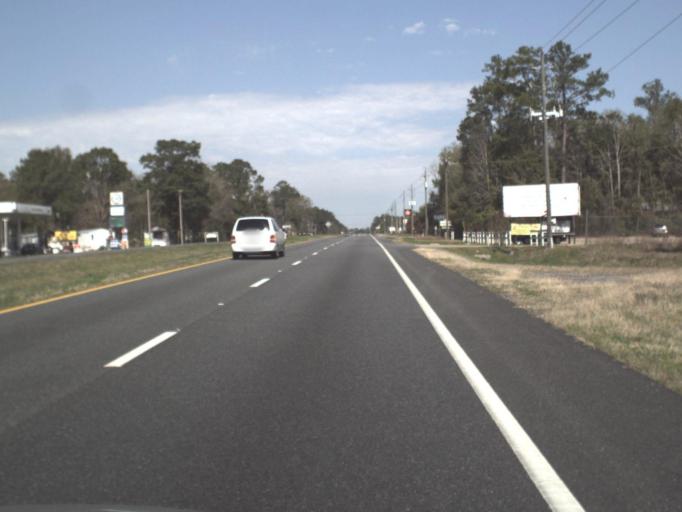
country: US
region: Florida
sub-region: Gadsden County
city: Havana
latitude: 30.5716
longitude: -84.3945
